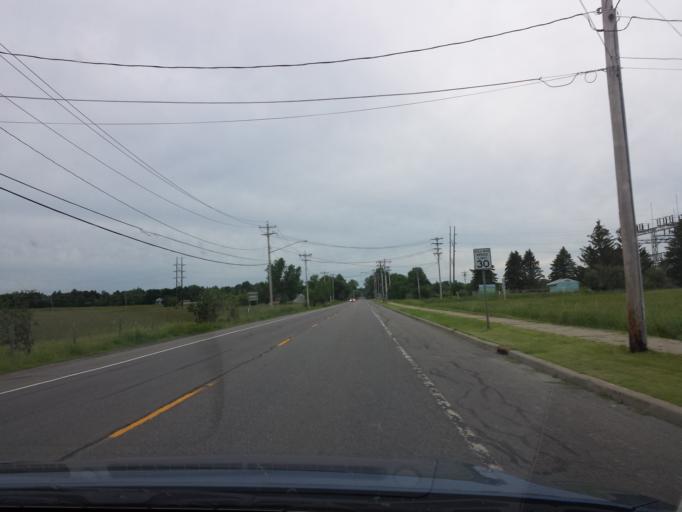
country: US
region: New York
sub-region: St. Lawrence County
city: Potsdam
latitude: 44.6793
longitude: -74.9688
